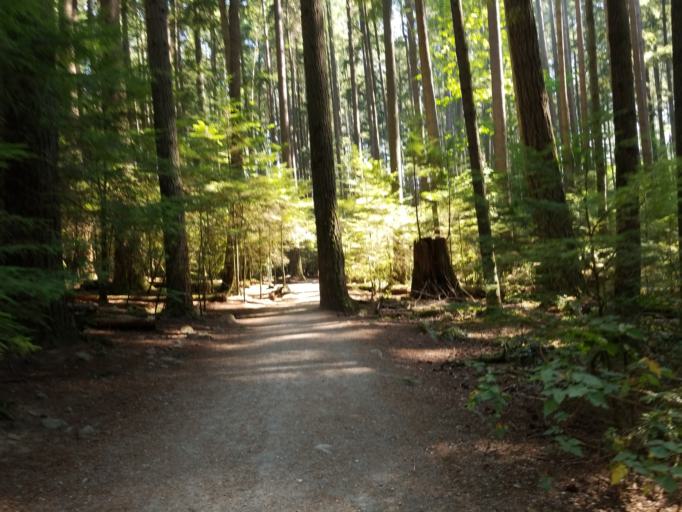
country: CA
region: British Columbia
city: West End
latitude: 49.2519
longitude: -123.2176
